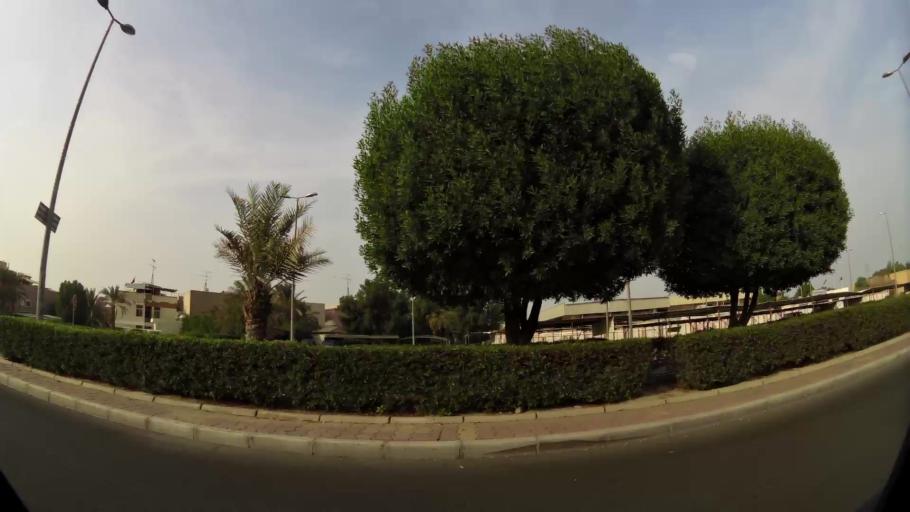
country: KW
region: Mubarak al Kabir
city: Sabah as Salim
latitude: 29.2568
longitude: 48.0526
